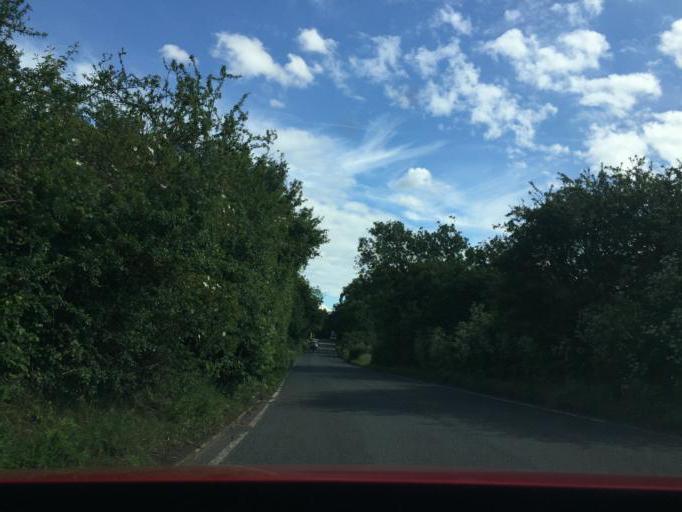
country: GB
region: England
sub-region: Hertfordshire
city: Codicote
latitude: 51.8563
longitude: -0.2394
